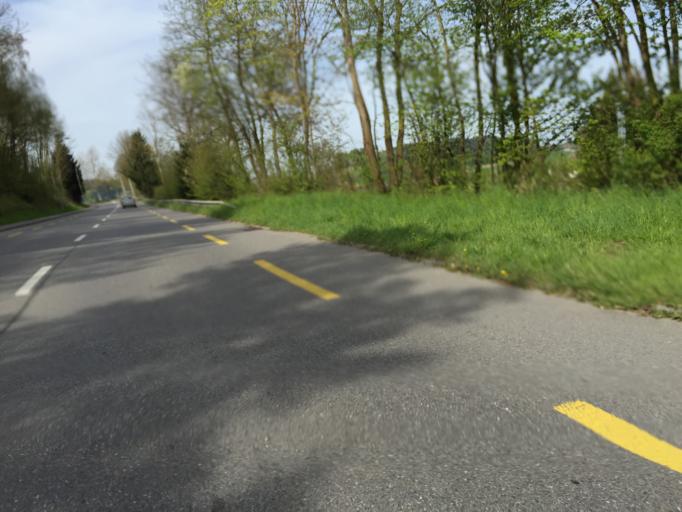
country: CH
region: Bern
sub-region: Bern-Mittelland District
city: Koniz
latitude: 46.9183
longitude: 7.4110
